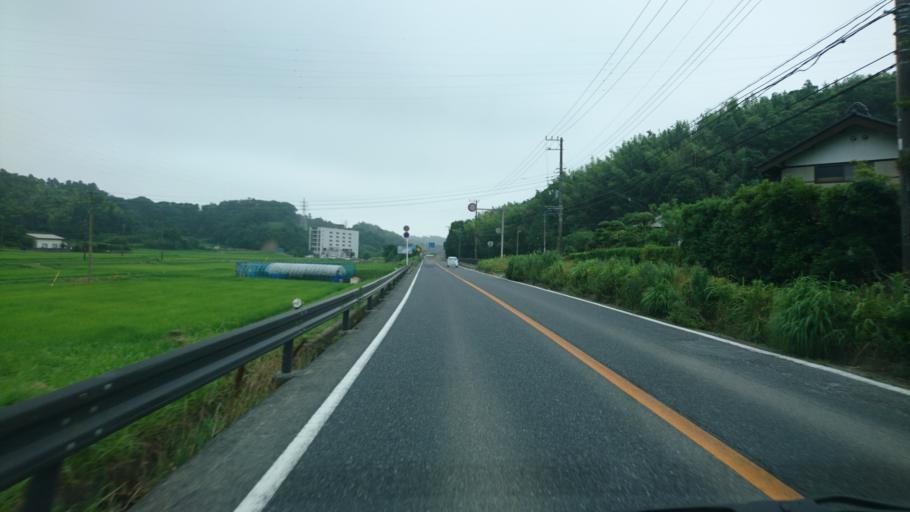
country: JP
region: Chiba
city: Kimitsu
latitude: 35.2698
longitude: 139.8959
